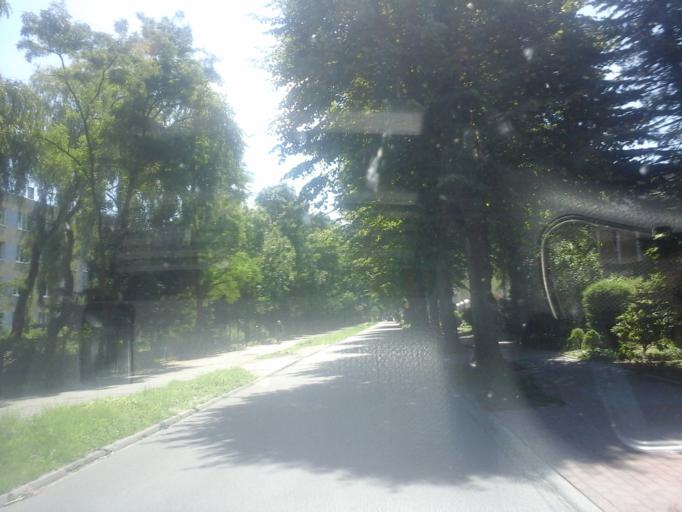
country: PL
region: West Pomeranian Voivodeship
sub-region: Powiat bialogardzki
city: Bialogard
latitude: 54.0123
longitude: 15.9902
